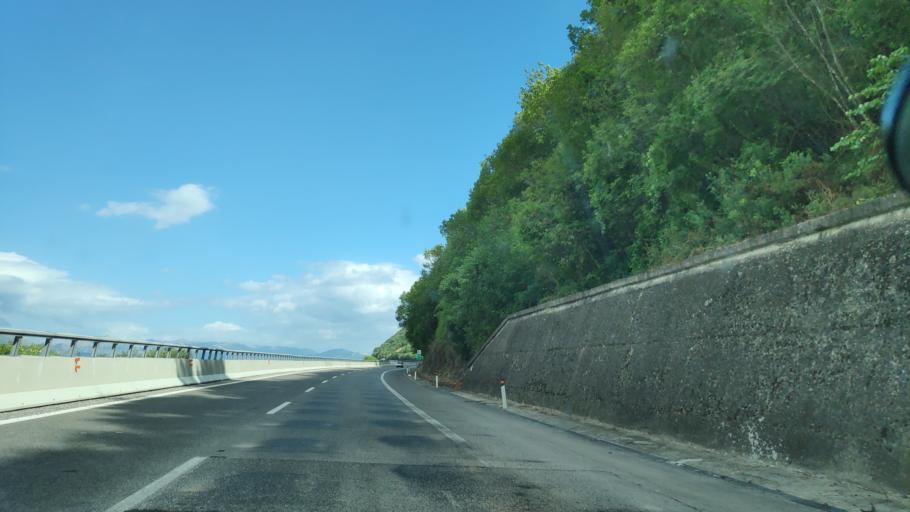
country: IT
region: Campania
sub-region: Provincia di Salerno
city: Sicignano degli Alburni
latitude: 40.5965
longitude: 15.3199
